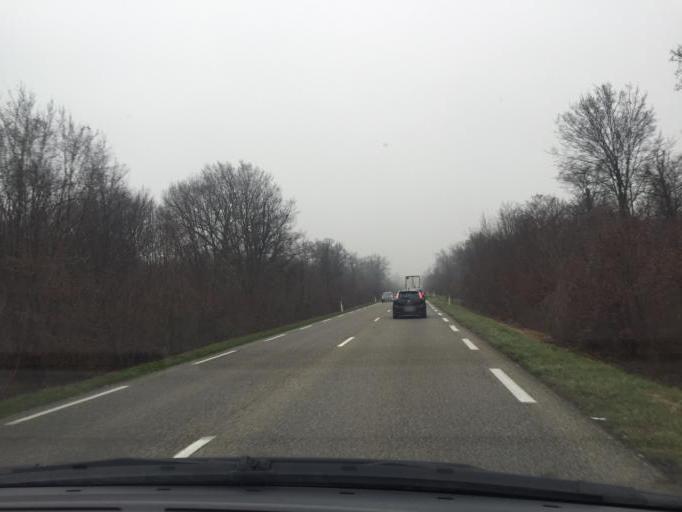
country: FR
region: Alsace
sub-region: Departement du Haut-Rhin
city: Widensolen
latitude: 48.0463
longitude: 7.4637
